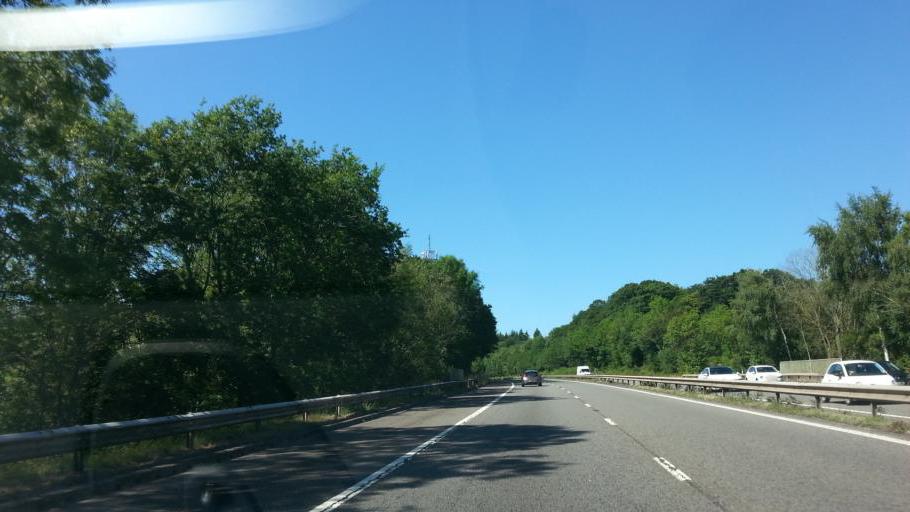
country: GB
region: England
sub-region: Gloucestershire
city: Newent
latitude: 51.9569
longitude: -2.4429
